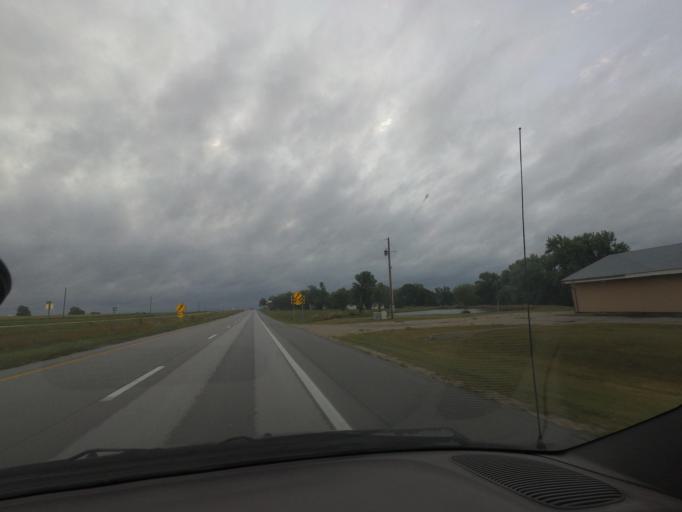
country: US
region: Missouri
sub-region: Shelby County
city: Shelbina
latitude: 39.6745
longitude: -91.9553
